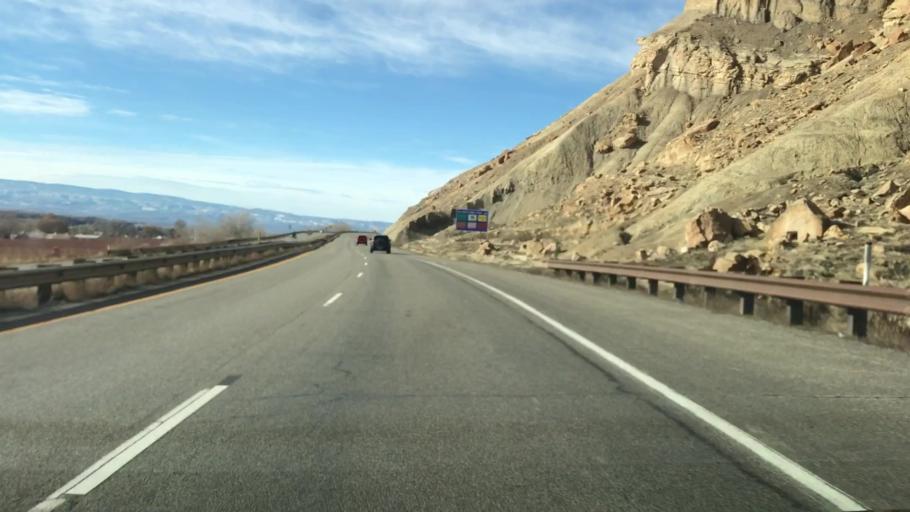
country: US
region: Colorado
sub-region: Mesa County
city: Palisade
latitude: 39.1193
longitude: -108.3410
